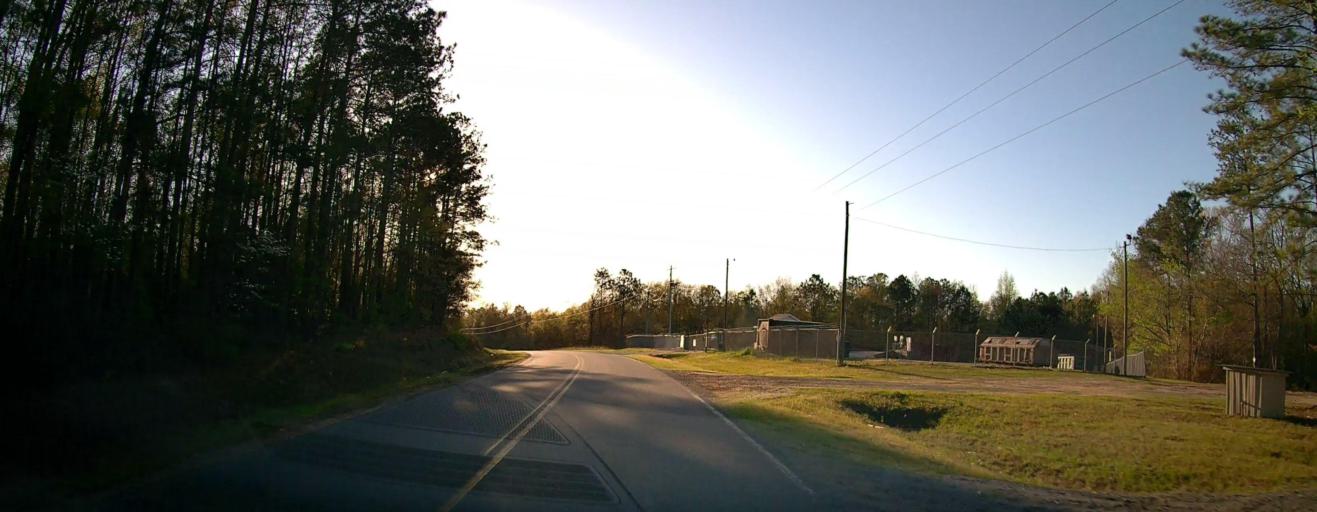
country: US
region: Georgia
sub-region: Wilkinson County
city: Gordon
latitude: 32.8832
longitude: -83.2846
